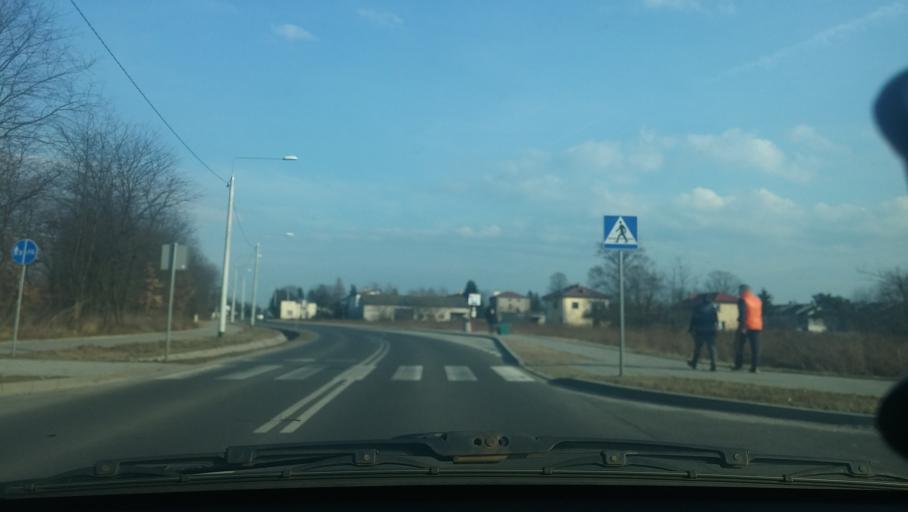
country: PL
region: Masovian Voivodeship
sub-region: Warszawa
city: Wawer
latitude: 52.1843
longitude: 21.1685
